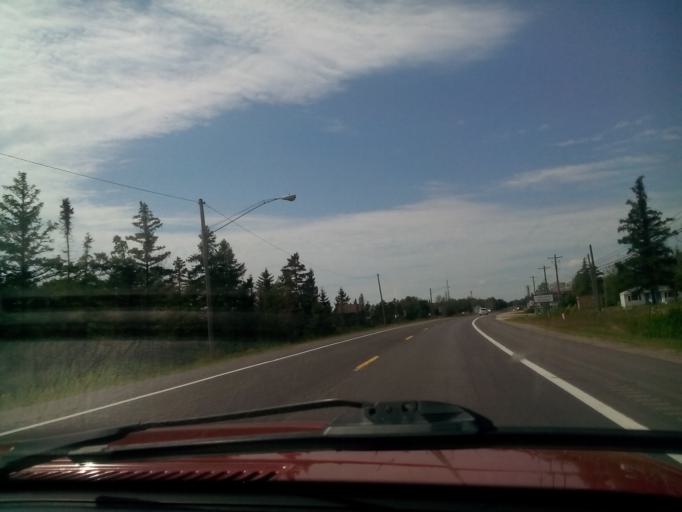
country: US
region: Michigan
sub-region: Schoolcraft County
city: Manistique
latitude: 45.9928
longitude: -86.0132
